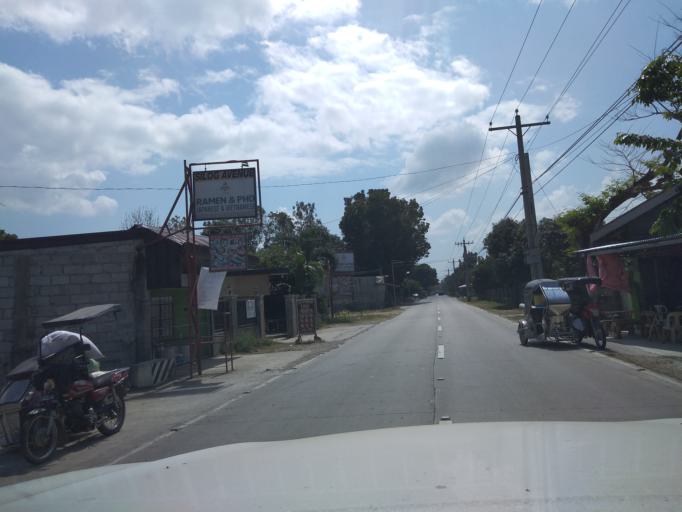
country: PH
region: Central Luzon
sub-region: Province of Pampanga
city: Lourdes
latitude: 15.0219
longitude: 120.8472
